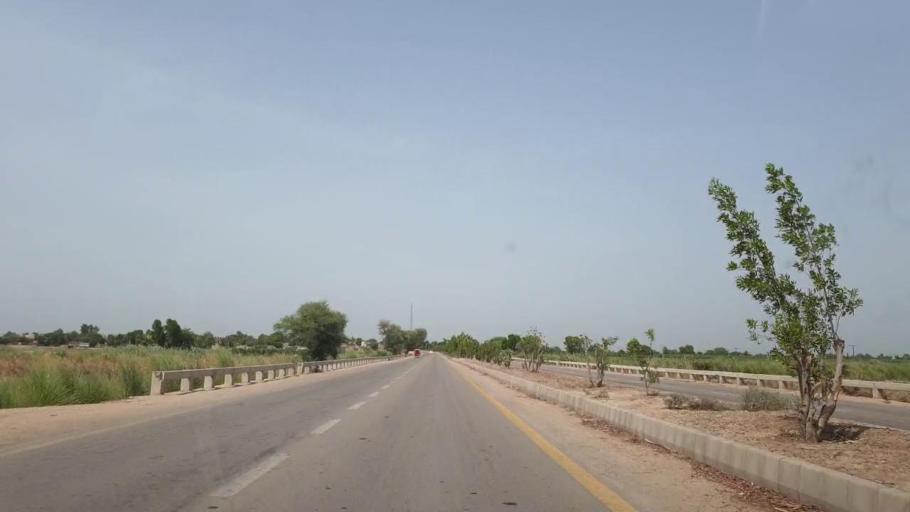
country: PK
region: Sindh
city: Sakrand
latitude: 26.1698
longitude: 68.2846
